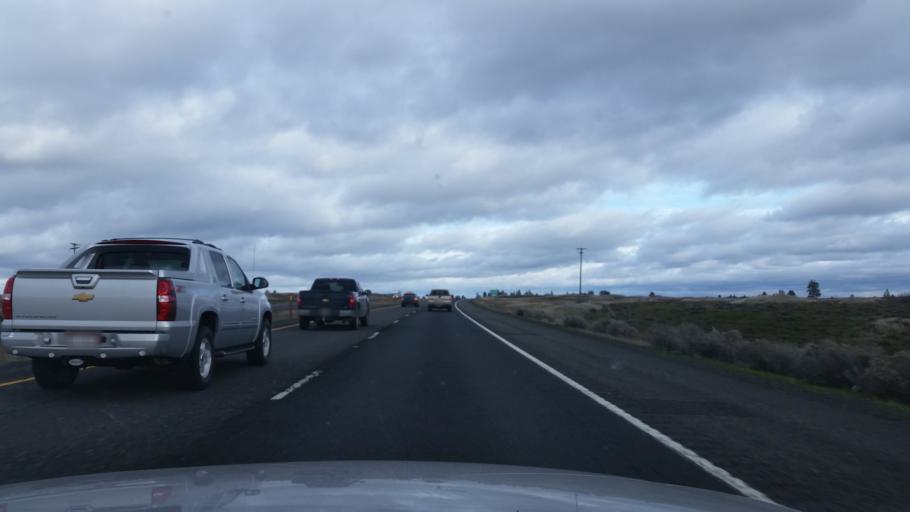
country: US
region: Washington
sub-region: Spokane County
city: Medical Lake
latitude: 47.3824
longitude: -117.8629
